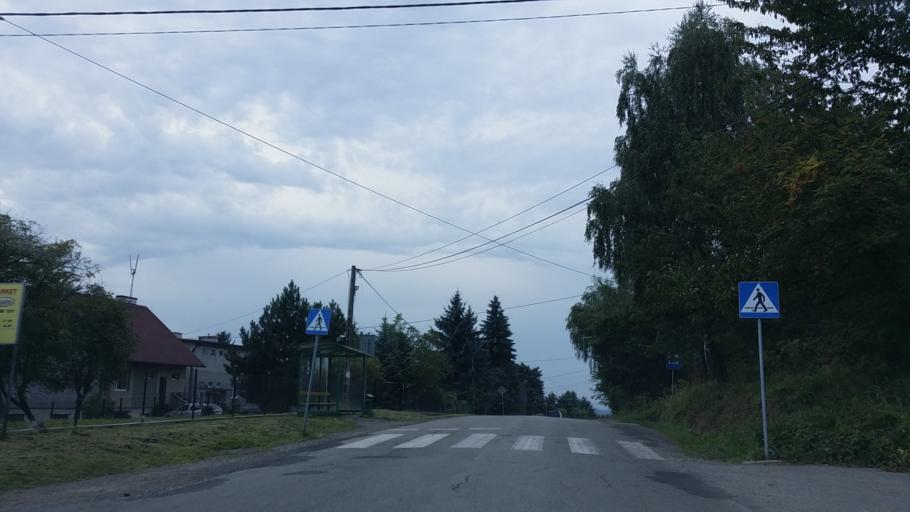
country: PL
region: Lesser Poland Voivodeship
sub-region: Powiat krakowski
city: Ochojno
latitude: 49.9744
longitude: 20.0114
